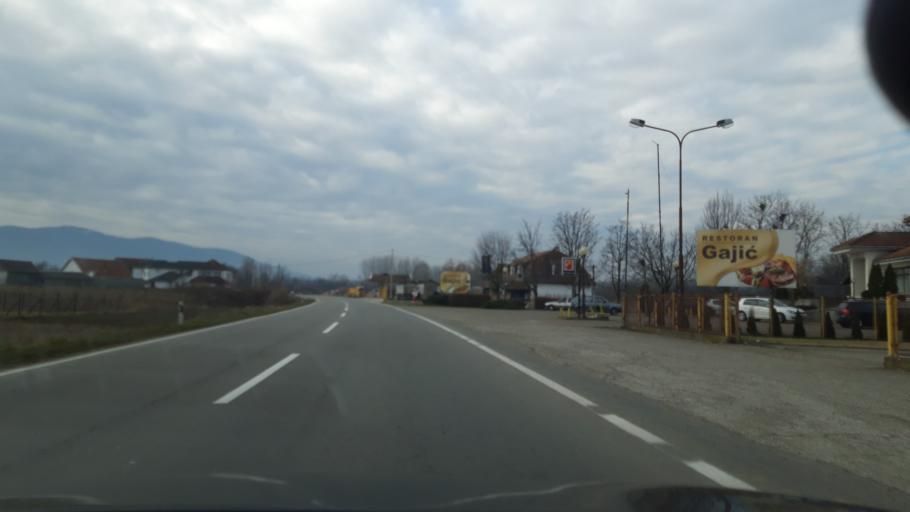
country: RS
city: Lipnicki Sor
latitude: 44.5654
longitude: 19.2024
